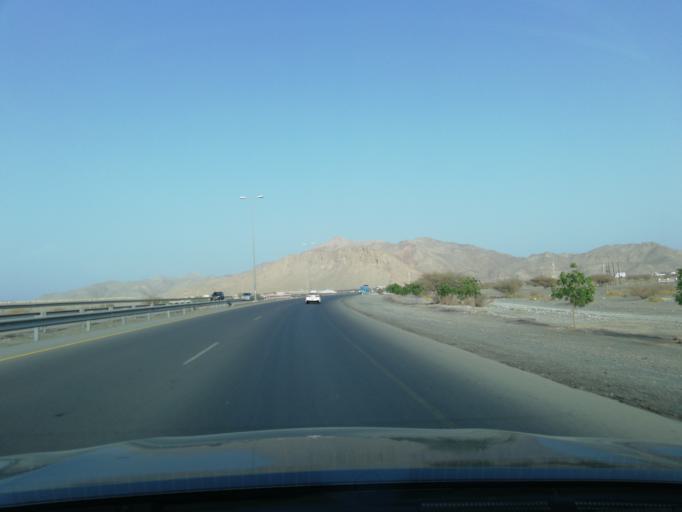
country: OM
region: Muhafazat ad Dakhiliyah
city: Nizwa
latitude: 22.8626
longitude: 57.5822
